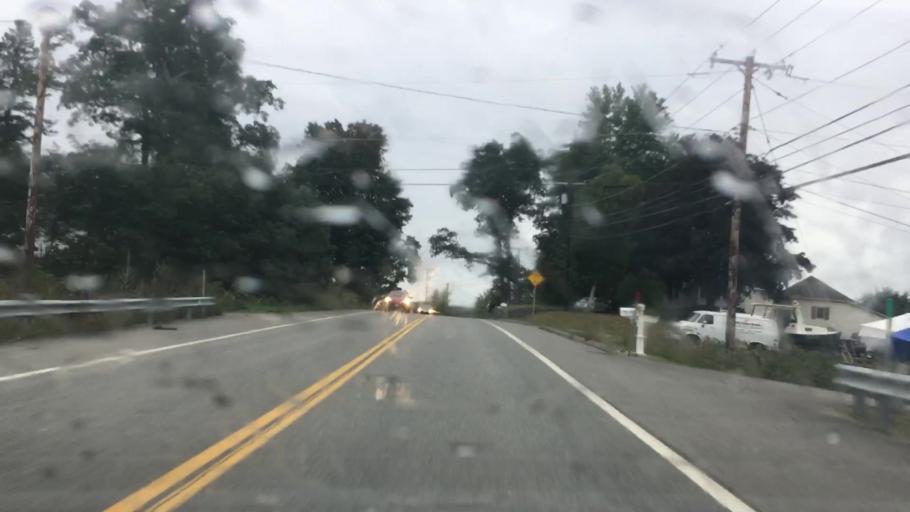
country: US
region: Maine
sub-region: Penobscot County
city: Orrington
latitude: 44.7240
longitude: -68.8267
